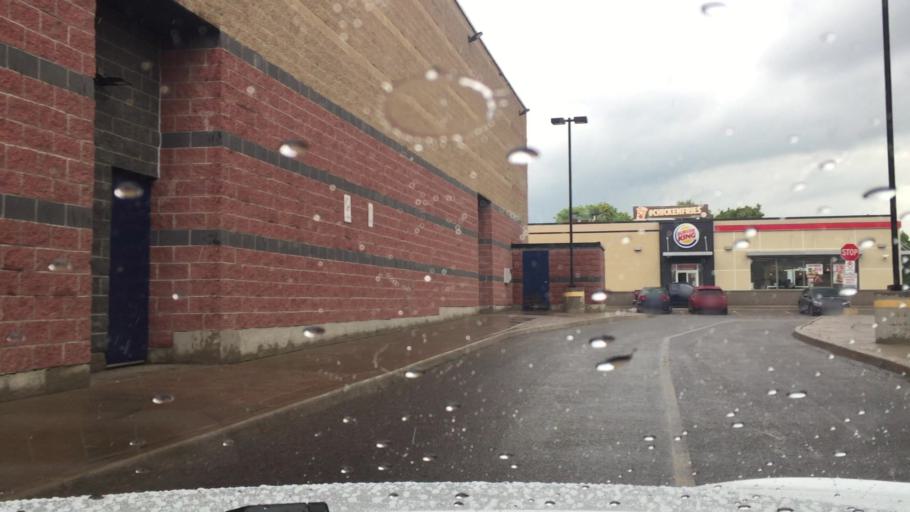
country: CA
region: Ontario
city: Oshawa
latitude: 43.9102
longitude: -78.7077
